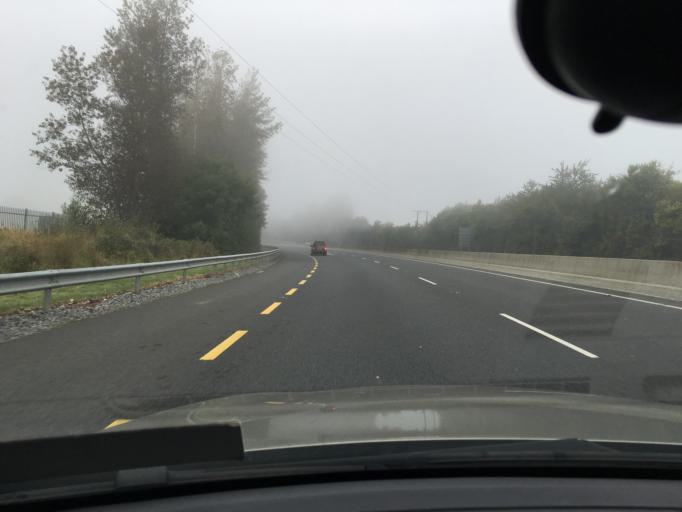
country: IE
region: Leinster
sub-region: An Iarmhi
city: Athlone
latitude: 53.4251
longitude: -7.8955
